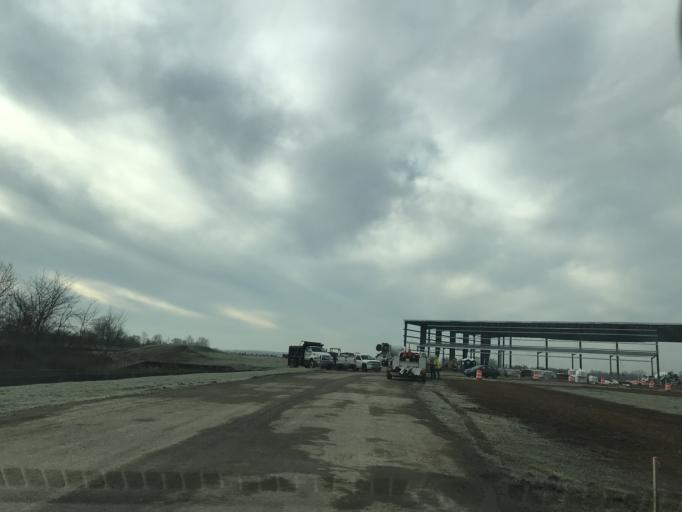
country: US
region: Virginia
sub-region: City of Manassas
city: Manassas
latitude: 38.7219
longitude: -77.5085
